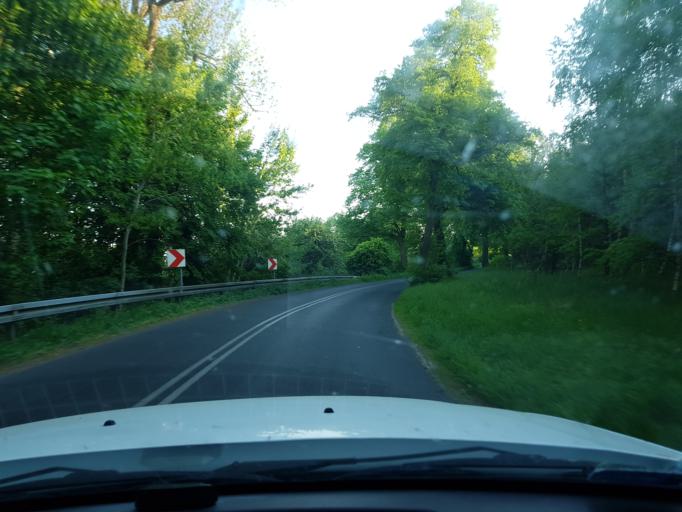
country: PL
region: West Pomeranian Voivodeship
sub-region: Powiat stargardzki
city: Kobylanka
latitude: 53.4333
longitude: 14.9030
